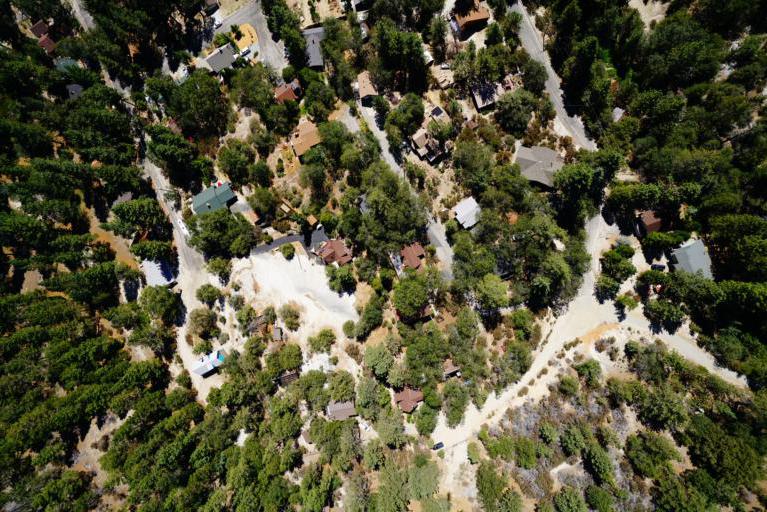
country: US
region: California
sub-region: Riverside County
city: Idyllwild-Pine Cove
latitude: 33.7588
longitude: -116.7306
